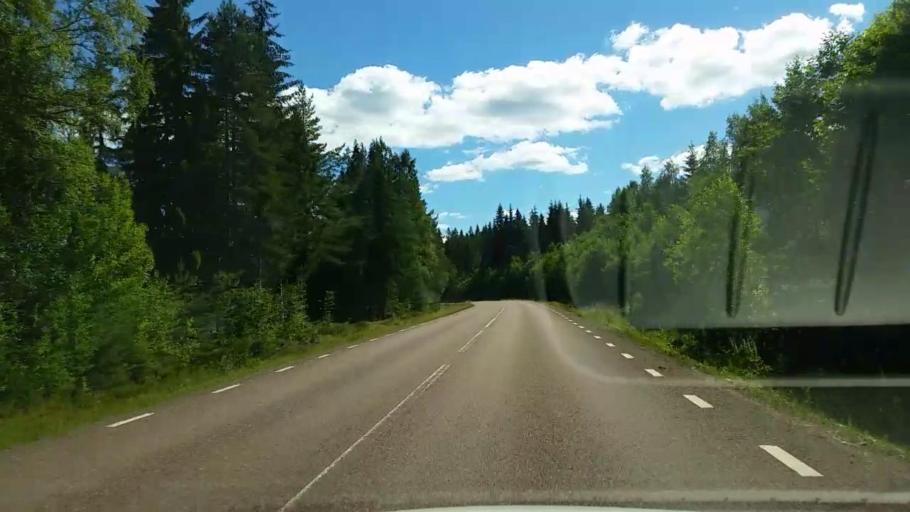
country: SE
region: Dalarna
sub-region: Faluns Kommun
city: Svardsjo
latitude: 60.9597
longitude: 15.6918
